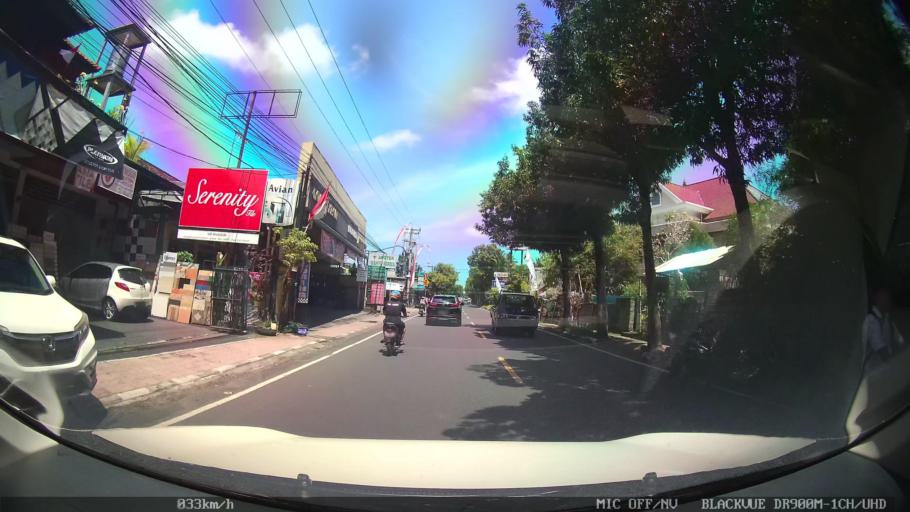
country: ID
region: Bali
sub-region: Kabupaten Gianyar
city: Ubud
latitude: -8.5543
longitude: 115.3028
